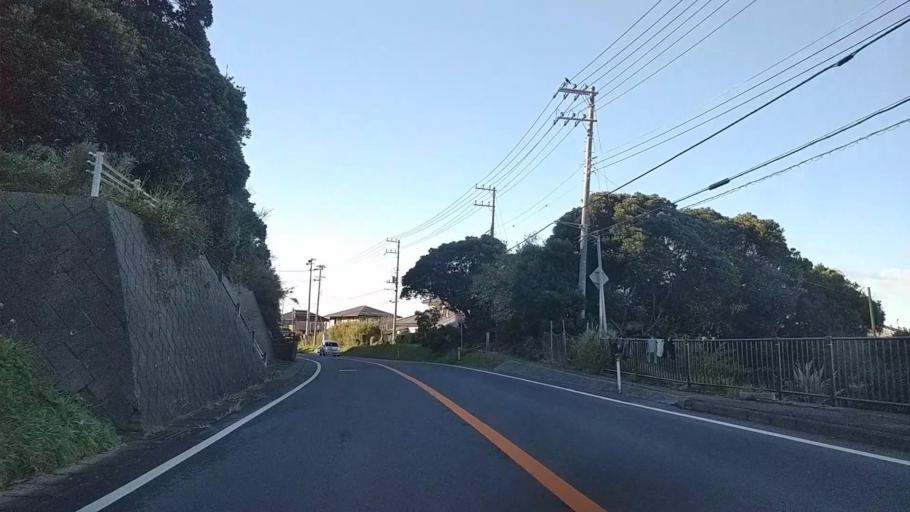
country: JP
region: Chiba
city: Futtsu
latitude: 35.2034
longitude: 139.8324
